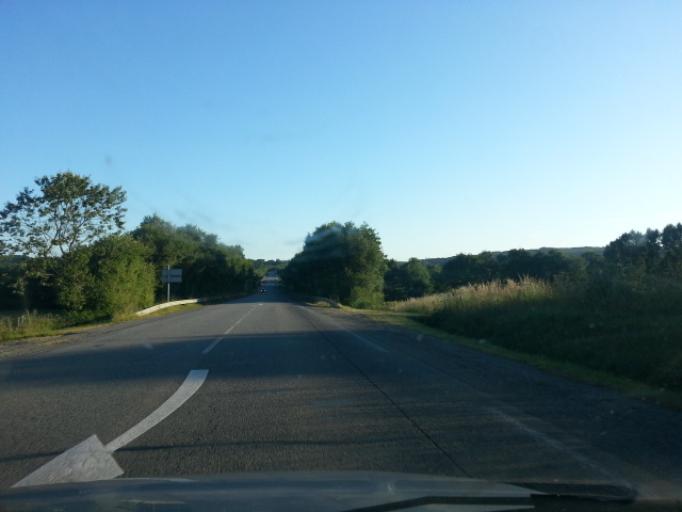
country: FR
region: Brittany
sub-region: Departement du Morbihan
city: Gourin
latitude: 48.1530
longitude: -3.5770
